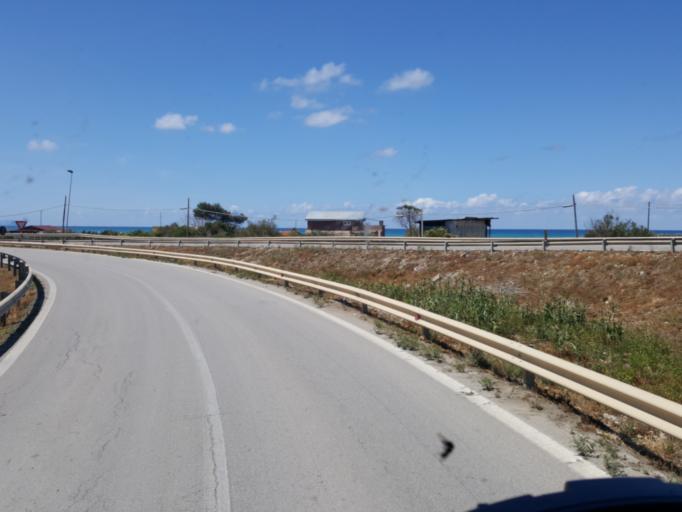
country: IT
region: Sicily
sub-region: Palermo
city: Cerda
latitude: 37.9754
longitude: 13.8079
